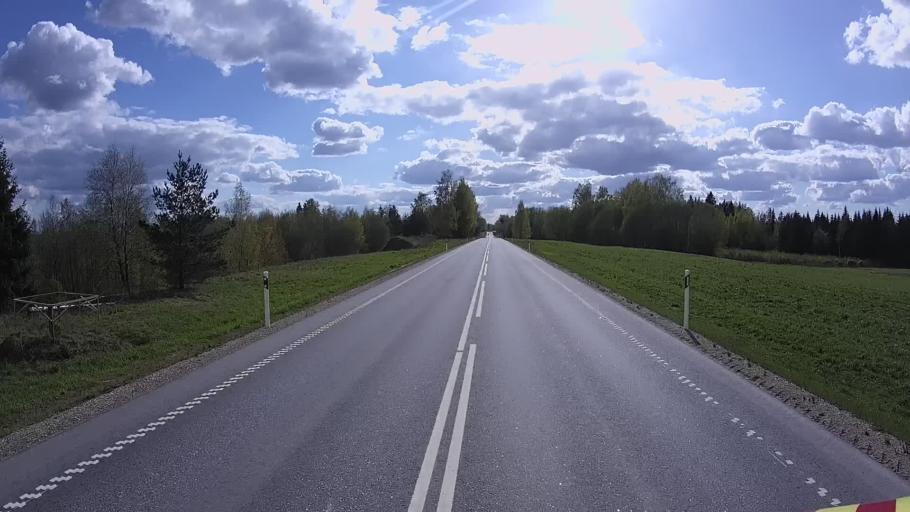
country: EE
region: Jogevamaa
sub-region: Mustvee linn
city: Mustvee
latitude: 58.8411
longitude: 26.8211
